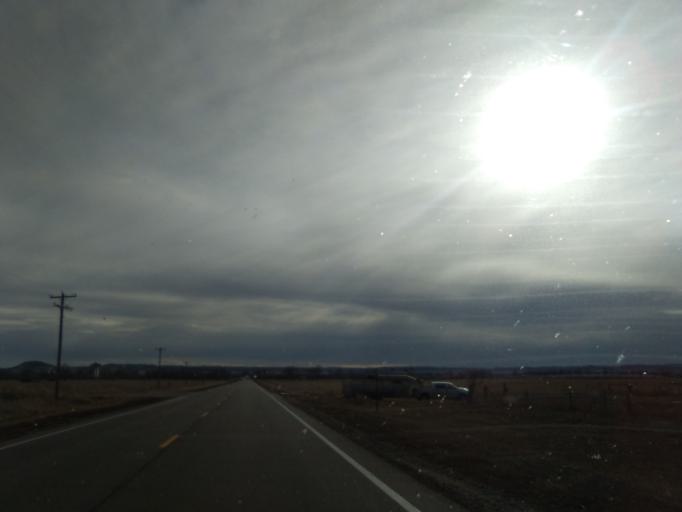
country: US
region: Nebraska
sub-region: Scotts Bluff County
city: Gering
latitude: 41.8013
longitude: -103.5192
